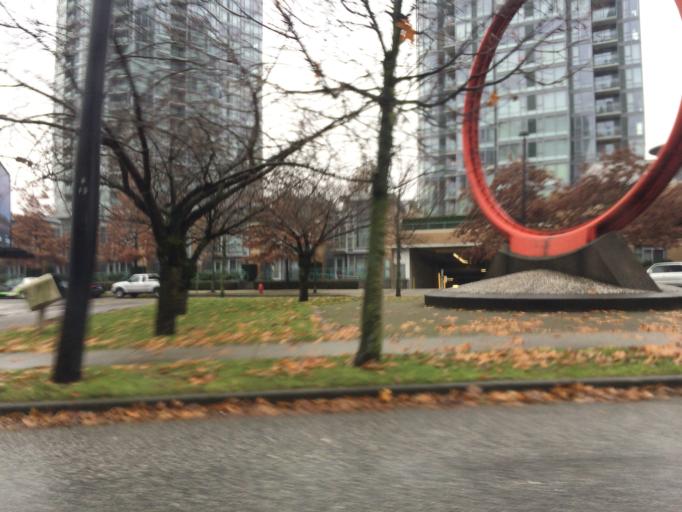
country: CA
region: British Columbia
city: West End
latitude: 49.2744
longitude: -123.1168
